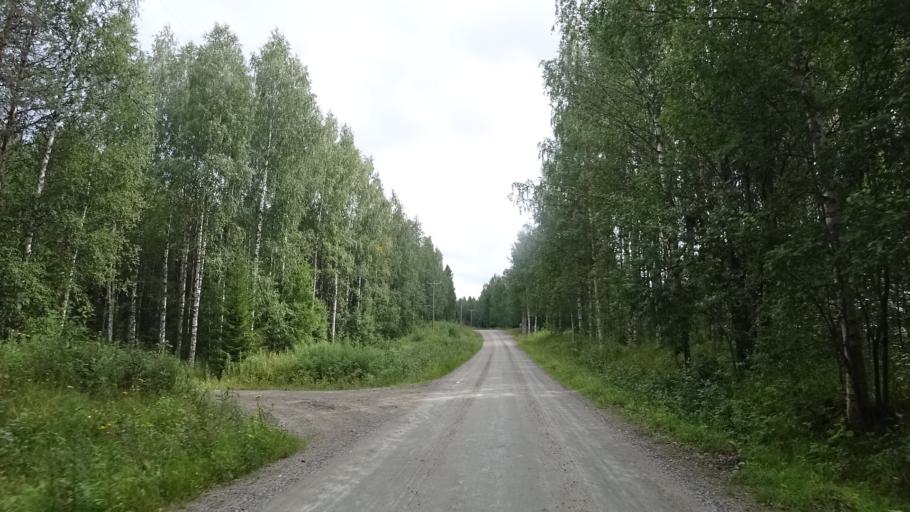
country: FI
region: North Karelia
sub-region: Joensuu
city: Ilomantsi
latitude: 62.9311
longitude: 31.3112
